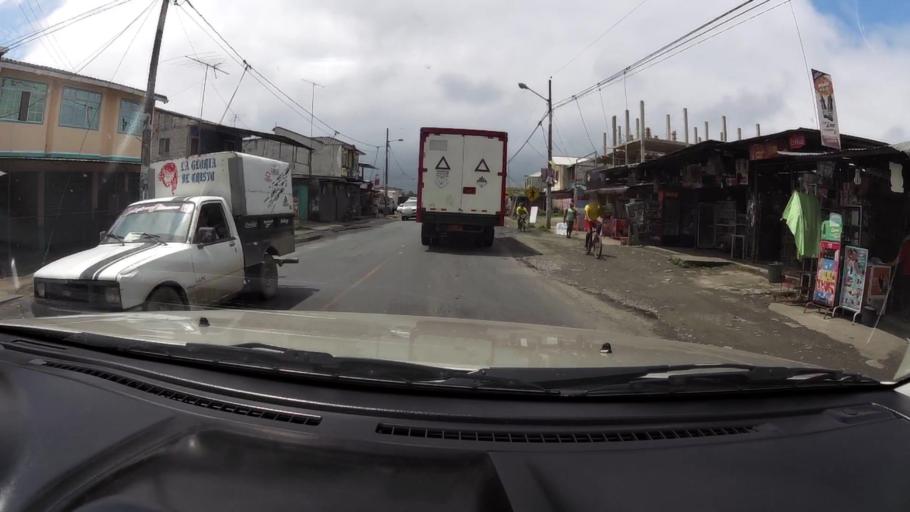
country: EC
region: Guayas
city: Balao
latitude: -2.9069
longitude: -79.7066
